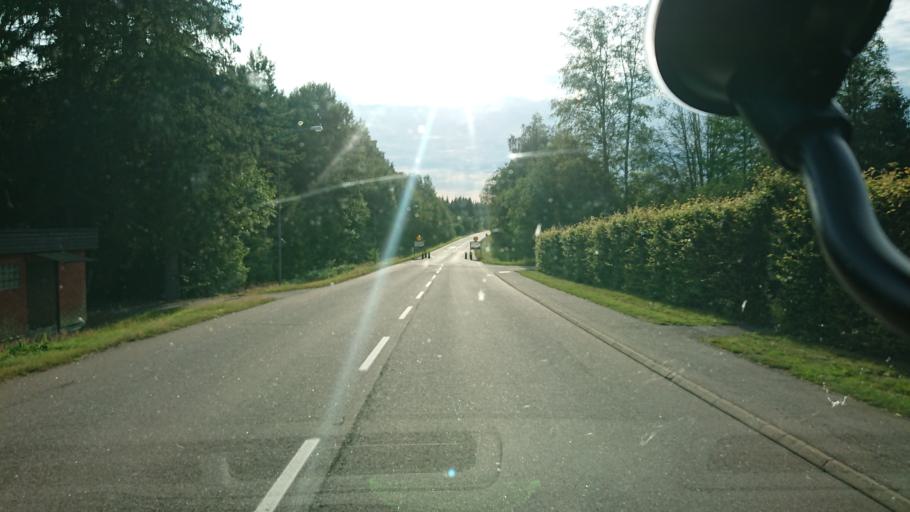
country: SE
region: Kronoberg
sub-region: Vaxjo Kommun
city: Rottne
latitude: 57.0341
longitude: 14.9334
